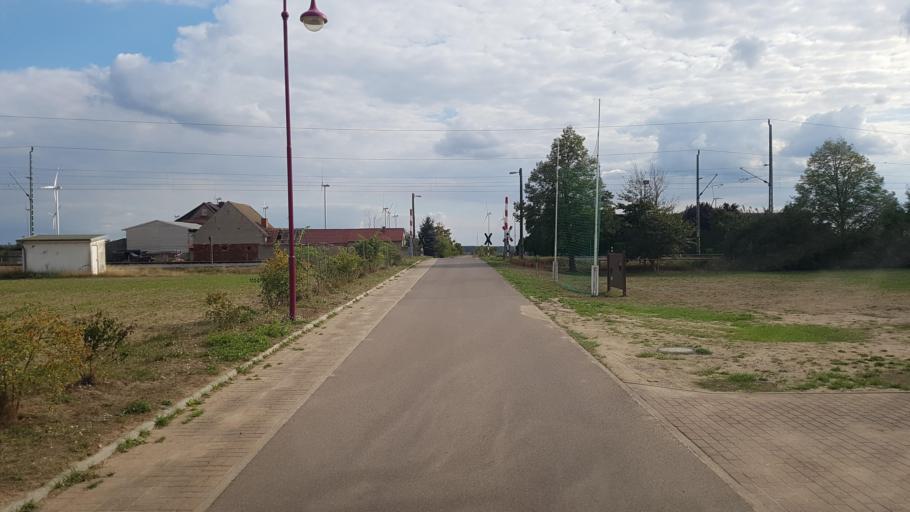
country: DE
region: Saxony
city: Arzberg
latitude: 51.5824
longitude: 13.1748
